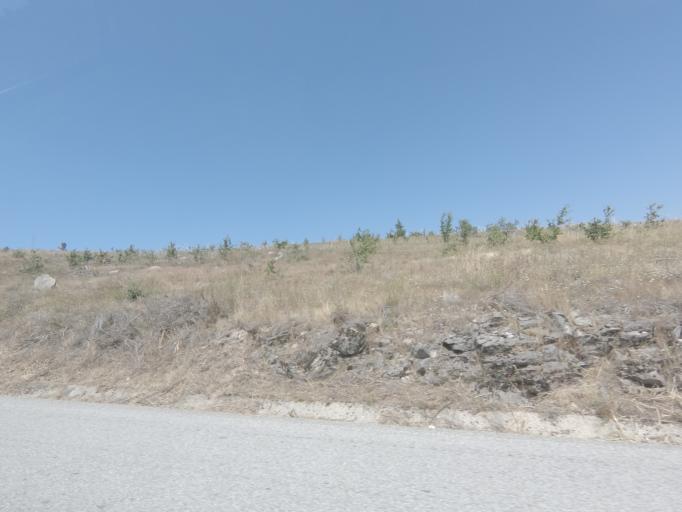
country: PT
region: Viseu
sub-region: Tarouca
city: Tarouca
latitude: 40.9844
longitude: -7.7954
